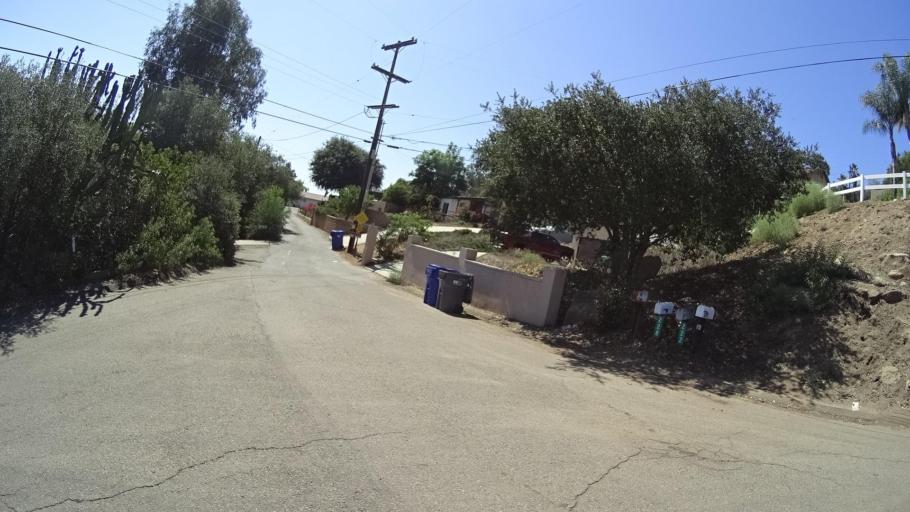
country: US
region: California
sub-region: San Diego County
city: Crest
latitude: 32.8083
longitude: -116.8606
